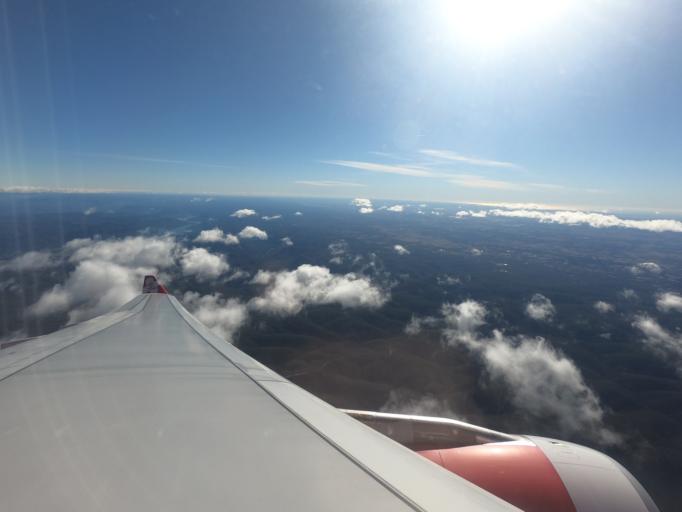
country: AU
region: New South Wales
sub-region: Wollondilly
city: Buxton
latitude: -34.2674
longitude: 150.4110
